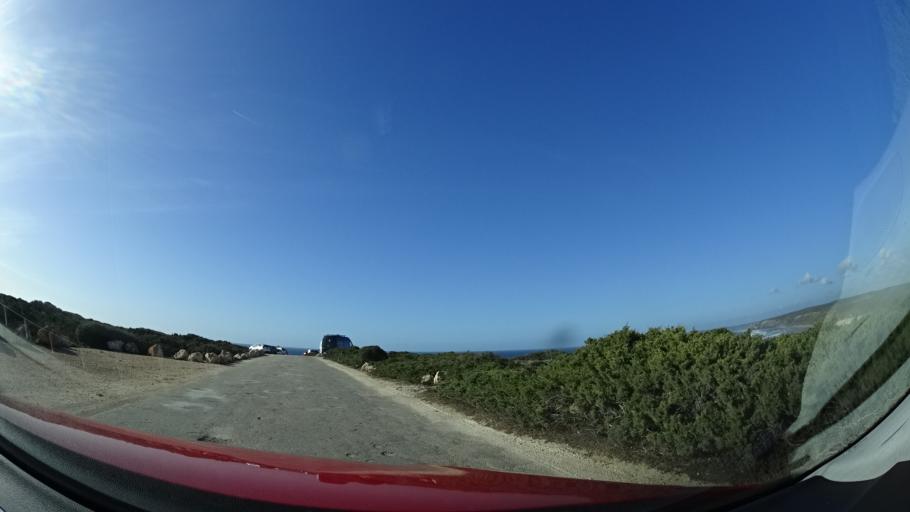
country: PT
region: Faro
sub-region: Vila do Bispo
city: Vila do Bispo
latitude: 37.1958
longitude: -8.9070
